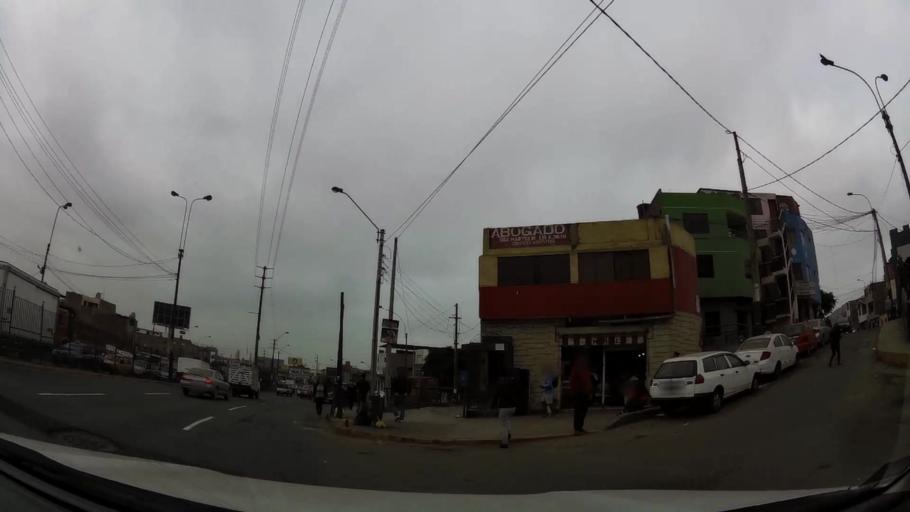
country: PE
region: Lima
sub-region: Lima
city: Surco
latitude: -12.1858
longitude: -77.0077
